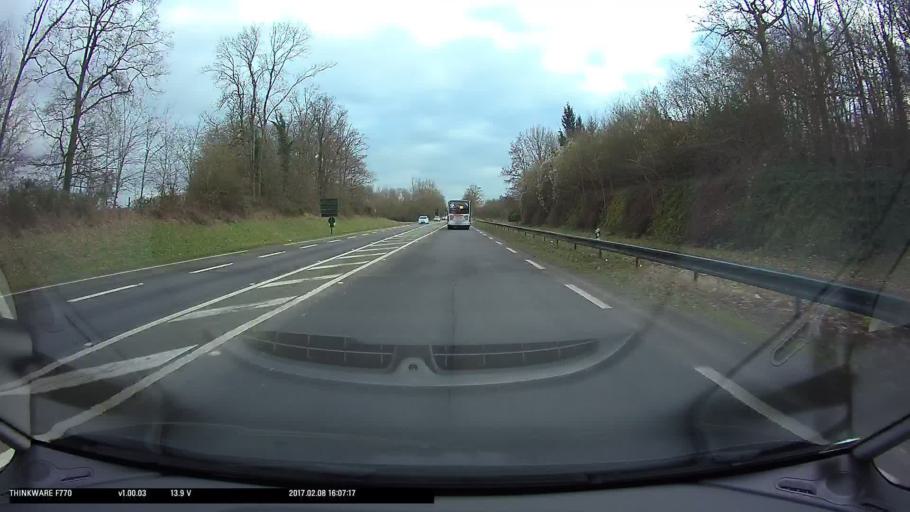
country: FR
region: Ile-de-France
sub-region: Departement du Val-d'Oise
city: Marines
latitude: 49.1311
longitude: 1.9941
